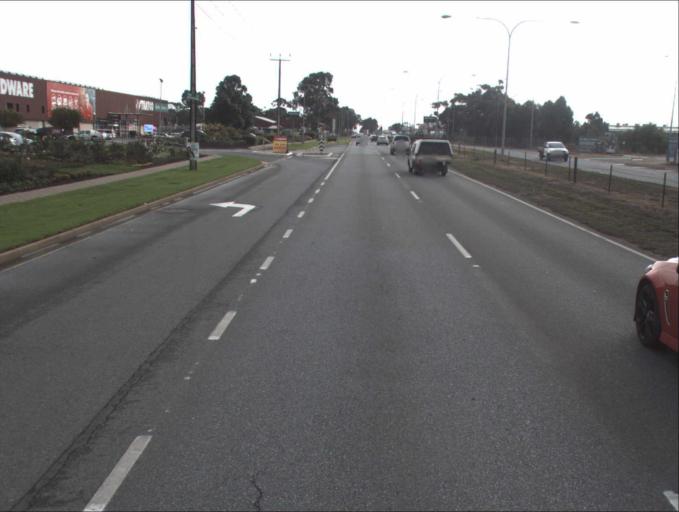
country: AU
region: South Australia
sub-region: Port Adelaide Enfield
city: Enfield
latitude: -34.8400
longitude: 138.5994
